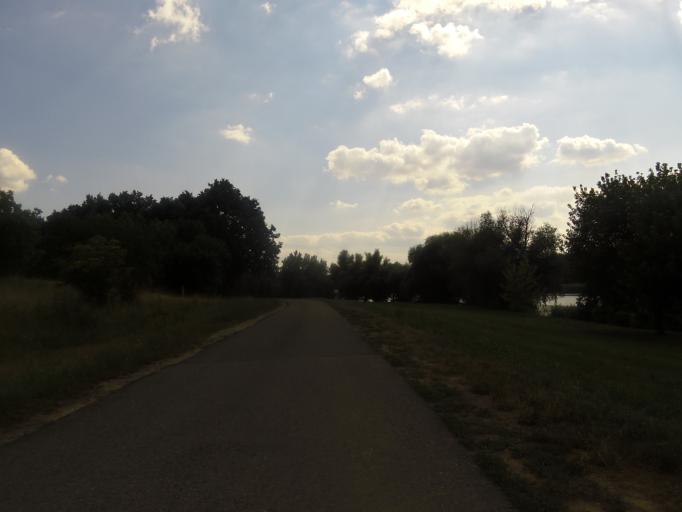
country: HU
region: Jasz-Nagykun-Szolnok
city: Tiszafured
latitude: 47.6188
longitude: 20.7266
